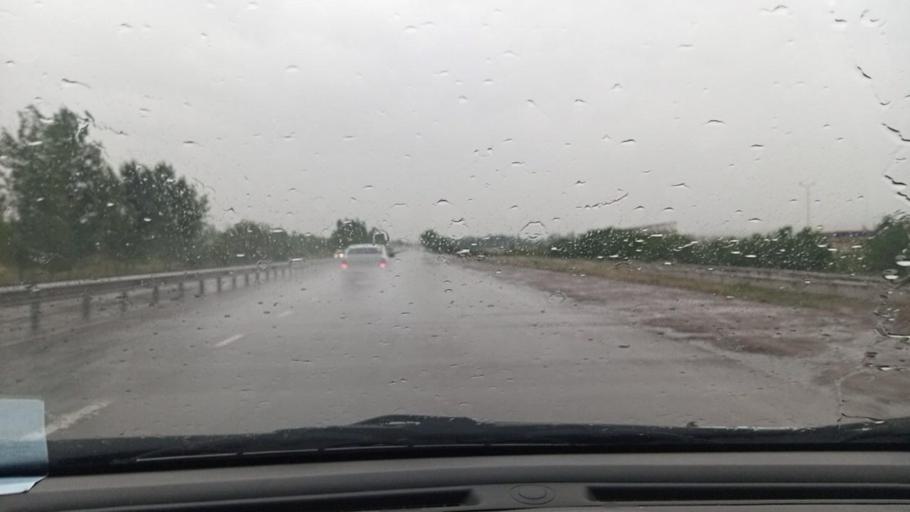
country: UZ
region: Toshkent
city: Ohangaron
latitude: 40.8991
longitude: 69.6726
